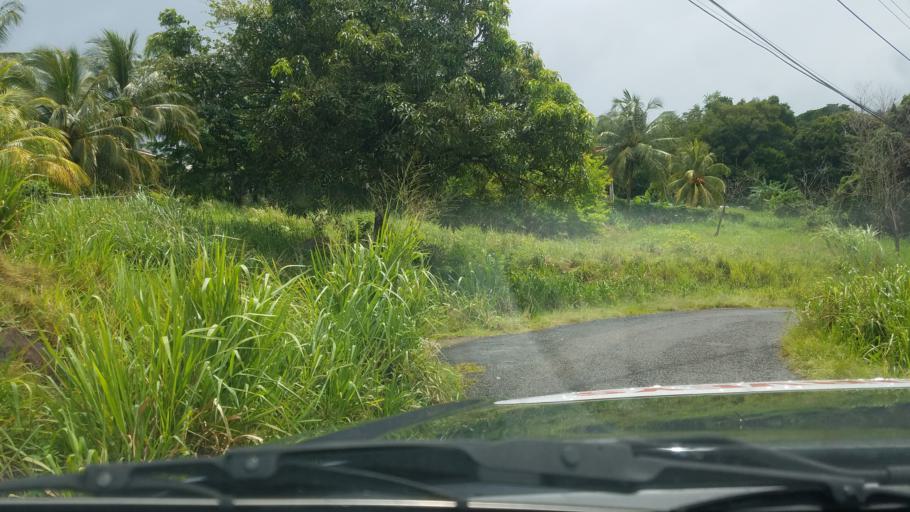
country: LC
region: Castries Quarter
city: Castries
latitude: 13.9949
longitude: -61.0021
